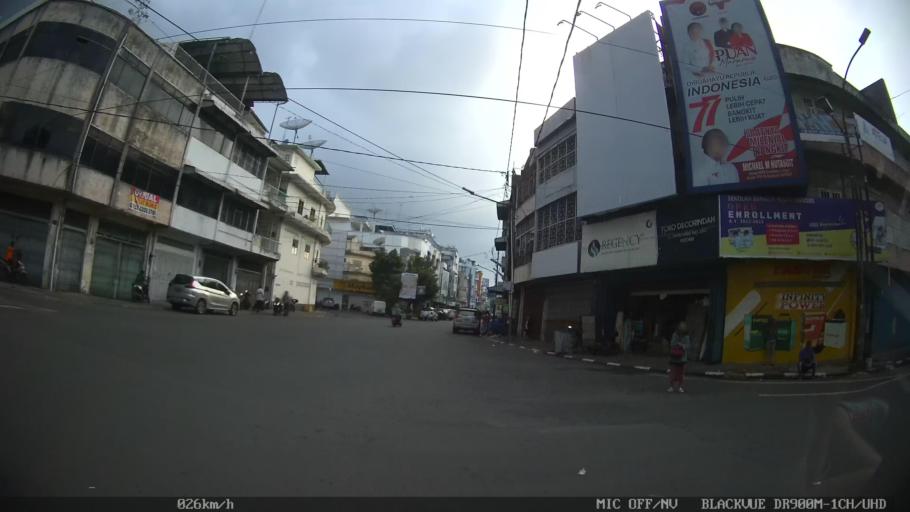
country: ID
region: North Sumatra
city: Medan
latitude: 3.5854
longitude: 98.6864
